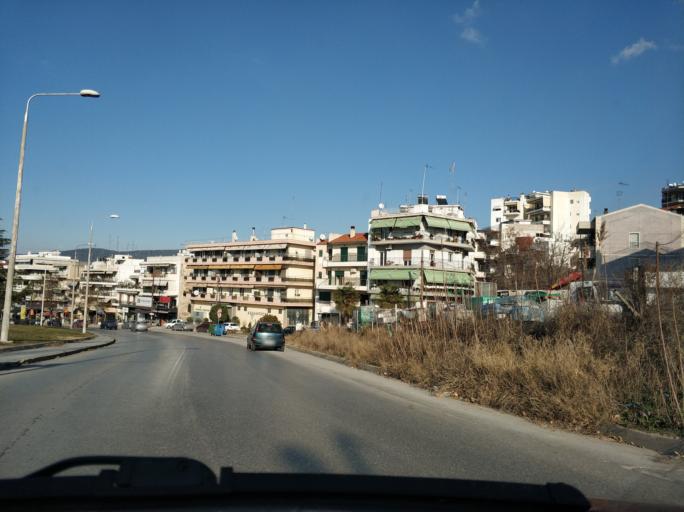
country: GR
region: Central Macedonia
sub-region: Nomos Thessalonikis
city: Pylaia
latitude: 40.5956
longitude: 22.9714
